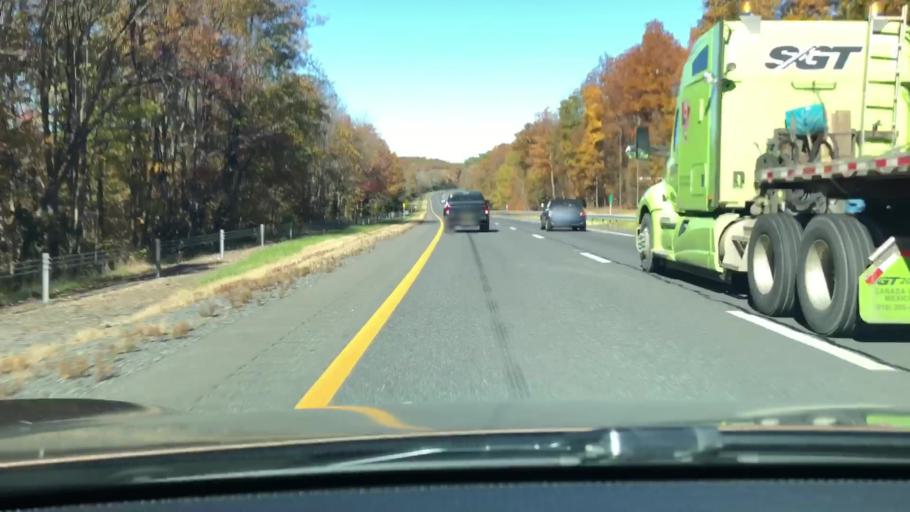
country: US
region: New York
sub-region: Ulster County
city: Tillson
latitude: 41.7887
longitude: -74.0501
